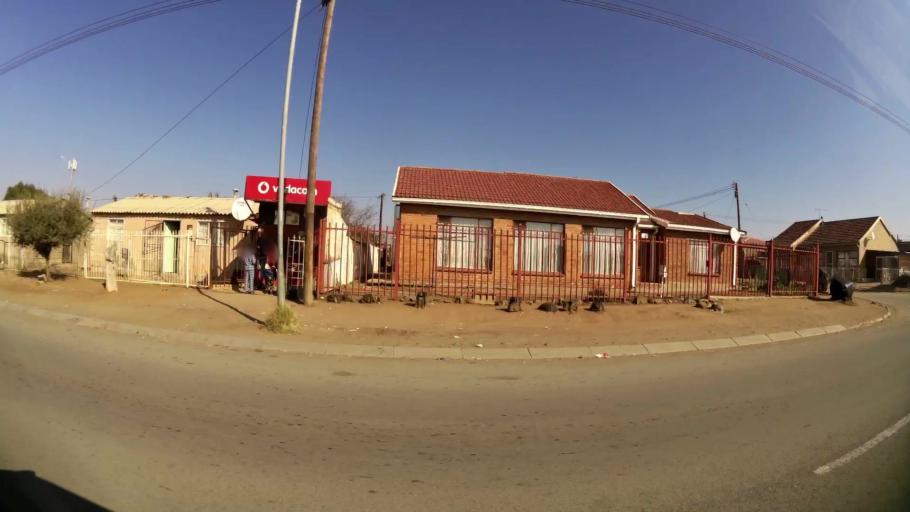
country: ZA
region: Orange Free State
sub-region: Mangaung Metropolitan Municipality
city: Bloemfontein
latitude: -29.1816
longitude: 26.2435
